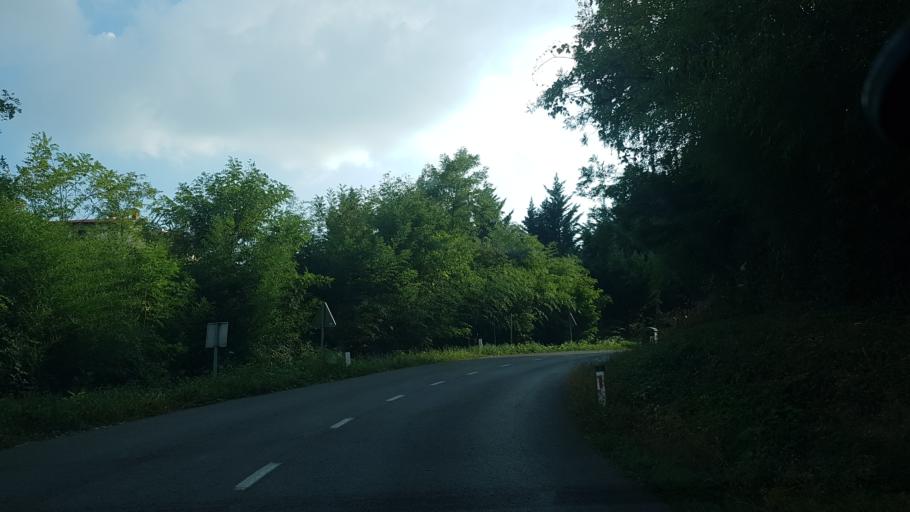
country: SI
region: Nova Gorica
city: Nova Gorica
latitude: 45.9478
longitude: 13.6444
